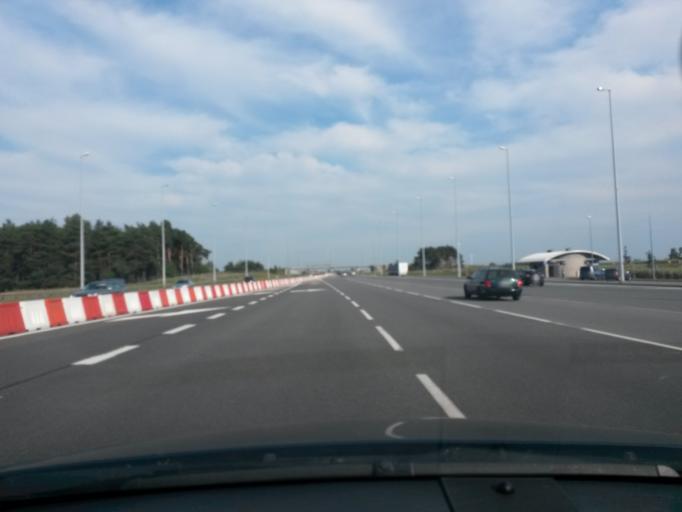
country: PL
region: Greater Poland Voivodeship
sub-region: Powiat slupecki
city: Ladek
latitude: 52.2215
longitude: 17.9521
